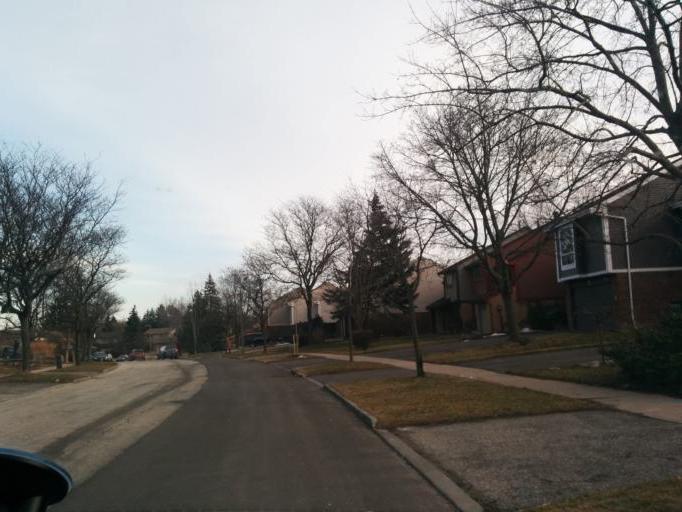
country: CA
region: Ontario
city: Mississauga
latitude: 43.5427
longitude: -79.6983
